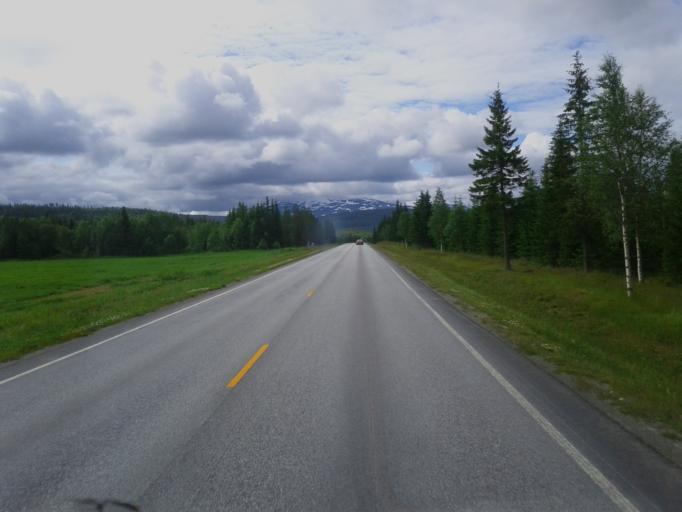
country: NO
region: Nord-Trondelag
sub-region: Namsskogan
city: Namsskogan
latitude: 64.7210
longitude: 12.8015
